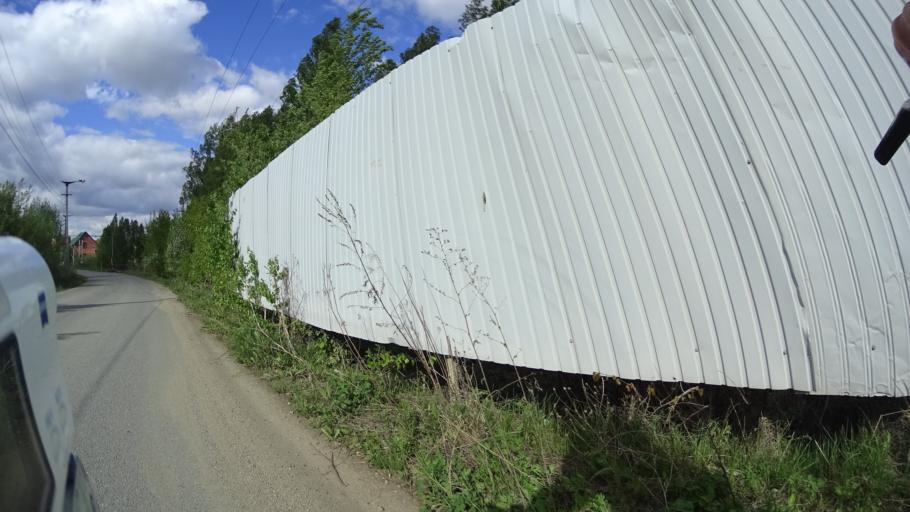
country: RU
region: Chelyabinsk
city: Sargazy
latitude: 55.1502
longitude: 61.2378
